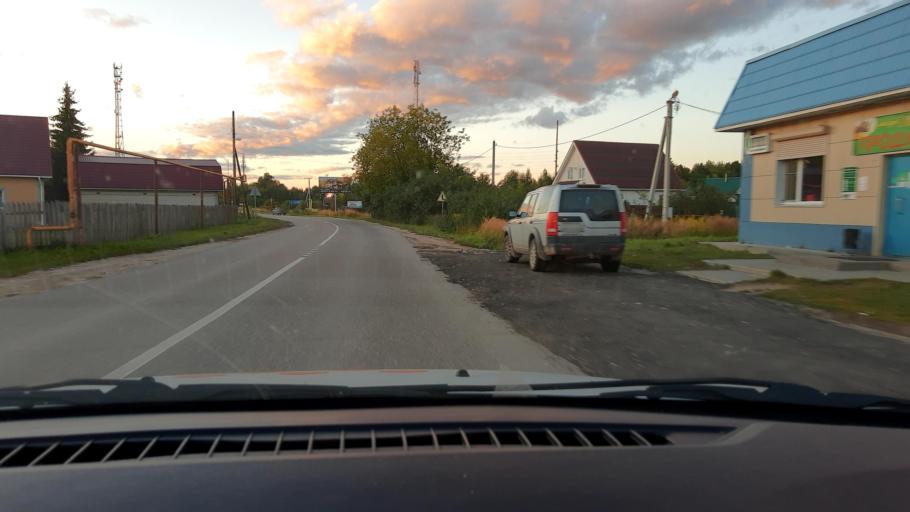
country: RU
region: Nizjnij Novgorod
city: Zavolzh'ye
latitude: 56.7110
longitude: 43.4161
